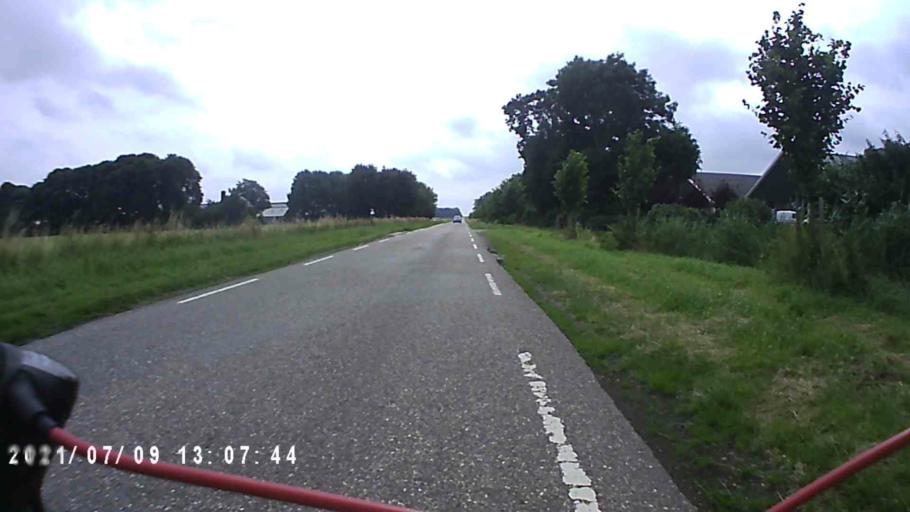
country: NL
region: Groningen
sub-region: Gemeente  Oldambt
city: Winschoten
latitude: 53.1320
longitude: 7.1072
